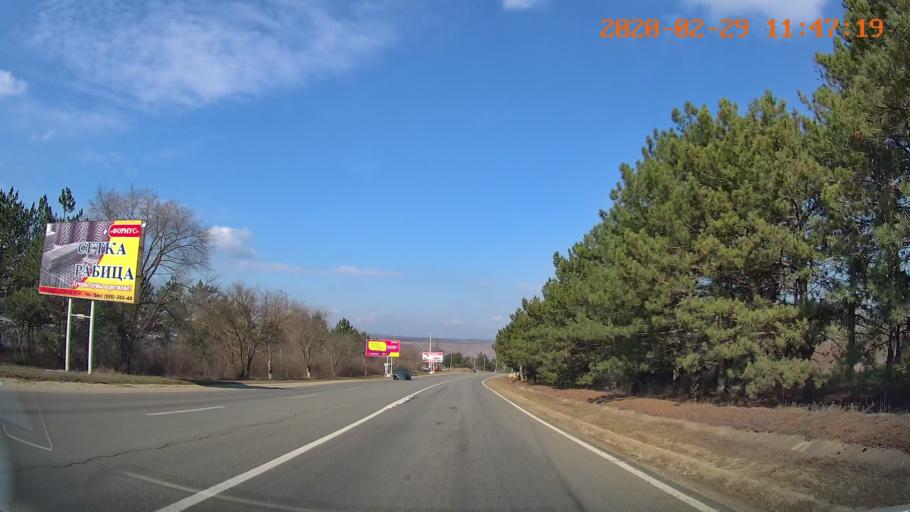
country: MD
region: Rezina
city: Rezina
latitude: 47.7394
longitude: 28.9887
